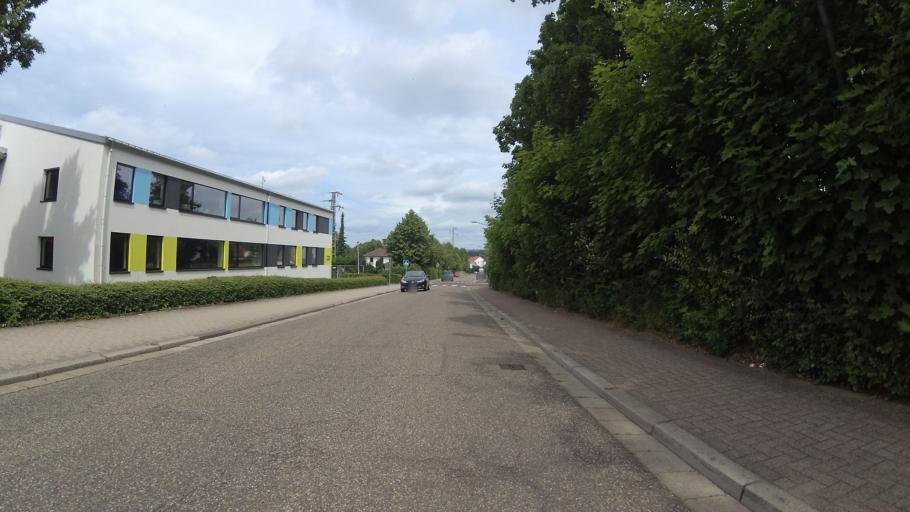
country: DE
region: Saarland
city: Spiesen-Elversberg
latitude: 49.2864
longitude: 7.1664
